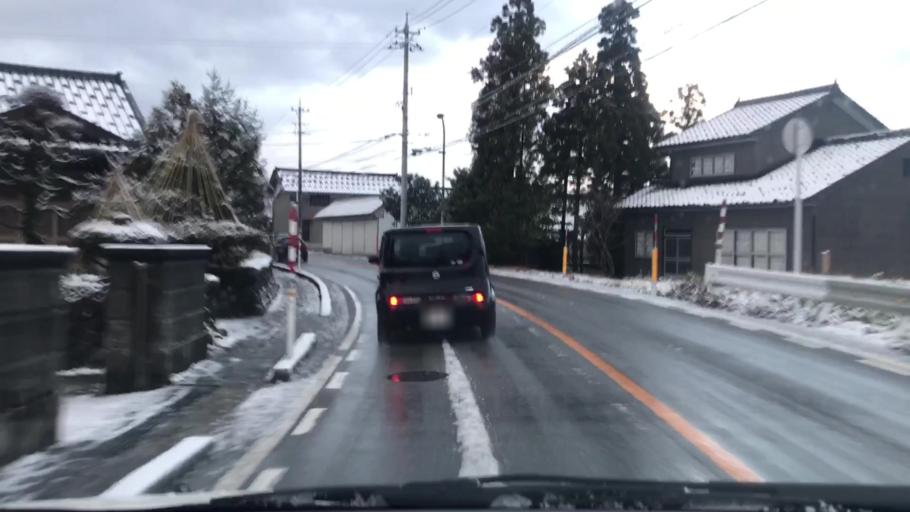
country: JP
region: Toyama
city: Kamiichi
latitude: 36.7038
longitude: 137.3146
